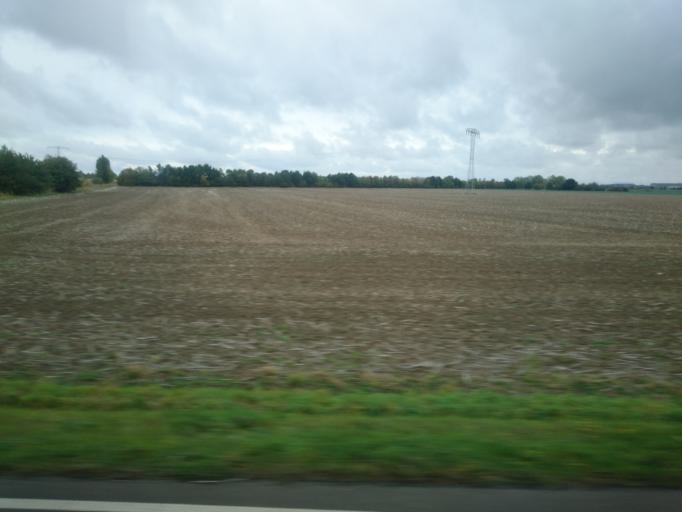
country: DE
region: Saxony-Anhalt
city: Ermlitz
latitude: 51.4063
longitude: 12.1664
